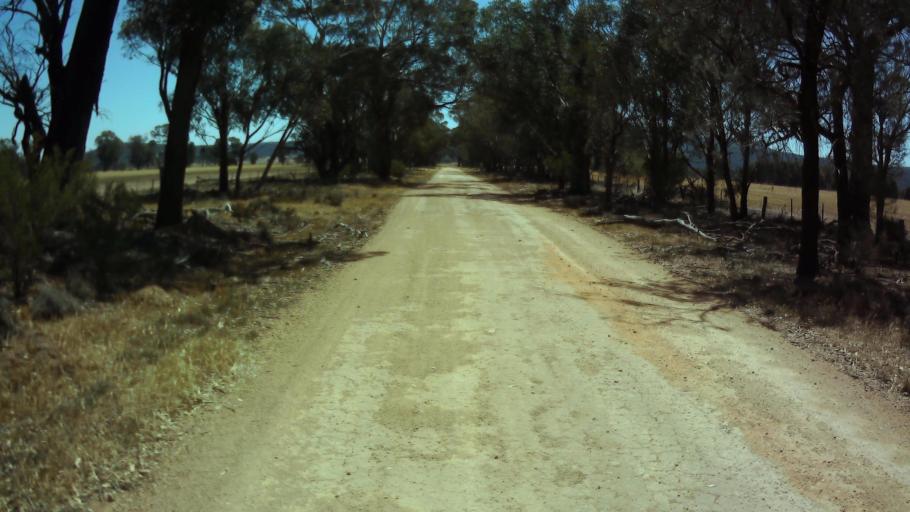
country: AU
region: New South Wales
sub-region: Weddin
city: Grenfell
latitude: -34.0117
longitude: 147.9636
